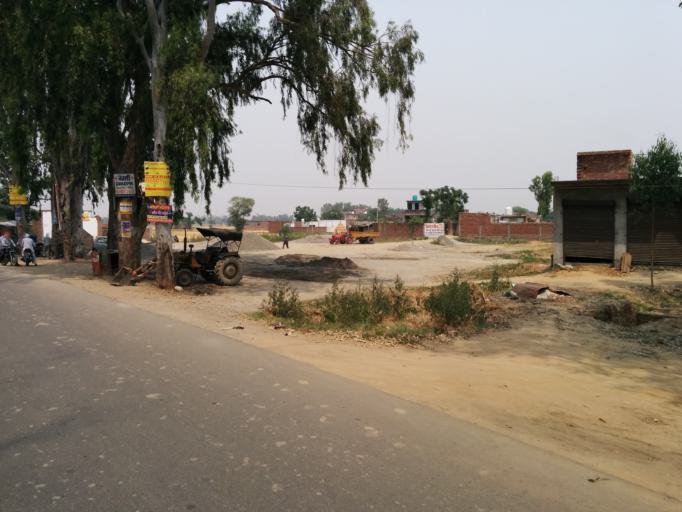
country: IN
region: Punjab
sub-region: Gurdaspur
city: Dhariwal
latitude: 31.9349
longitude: 75.3072
